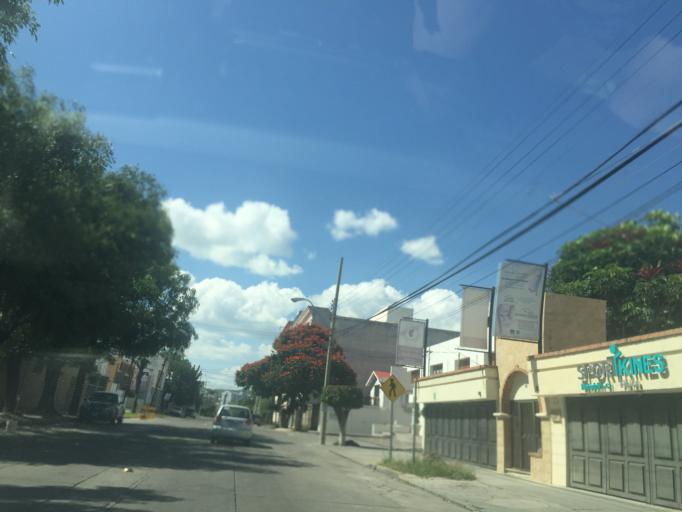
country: MX
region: Guanajuato
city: Leon
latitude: 21.1482
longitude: -101.6944
